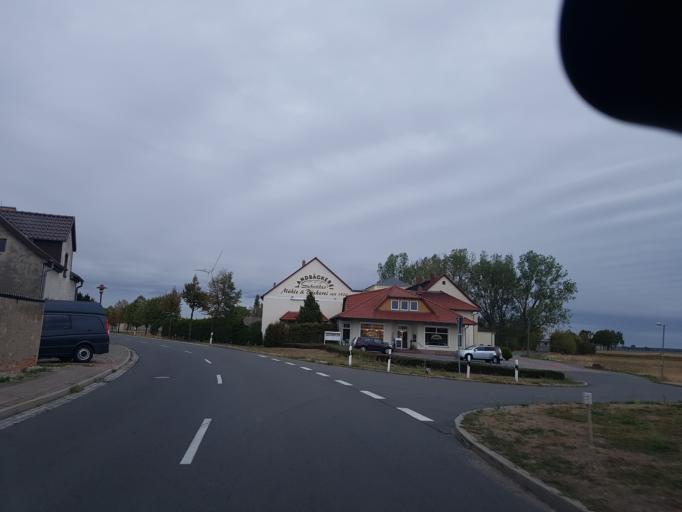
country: DE
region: Saxony-Anhalt
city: Prettin
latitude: 51.6481
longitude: 12.9788
